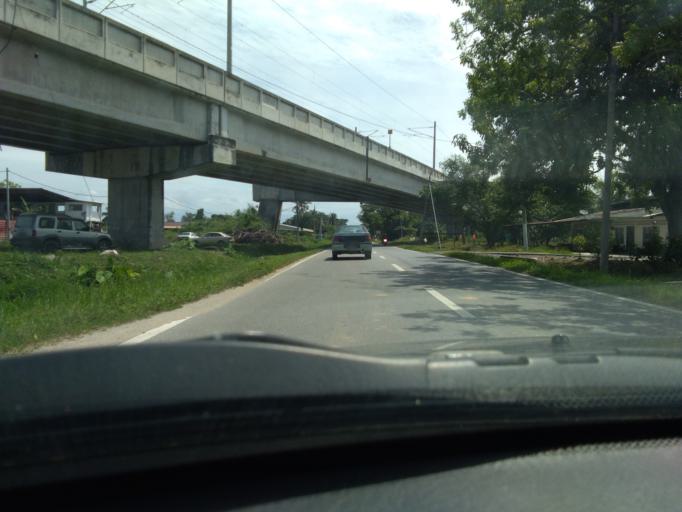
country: MY
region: Perak
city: Bagan Serai
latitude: 5.0186
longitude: 100.5447
